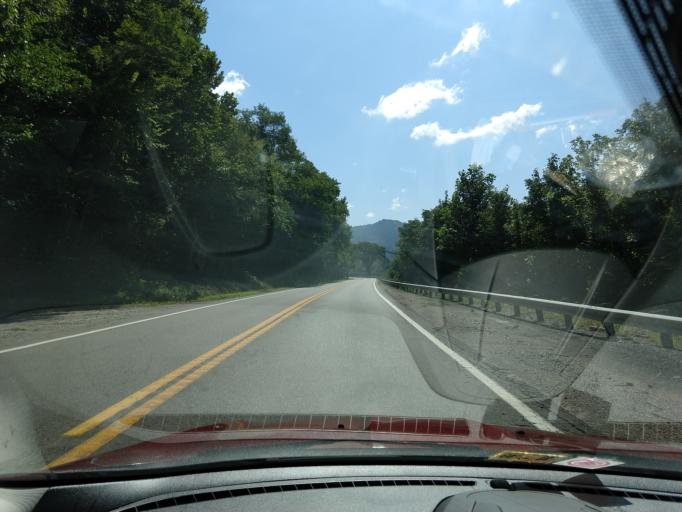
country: US
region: West Virginia
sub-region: Kanawha County
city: Montgomery
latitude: 38.1873
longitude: -81.3503
